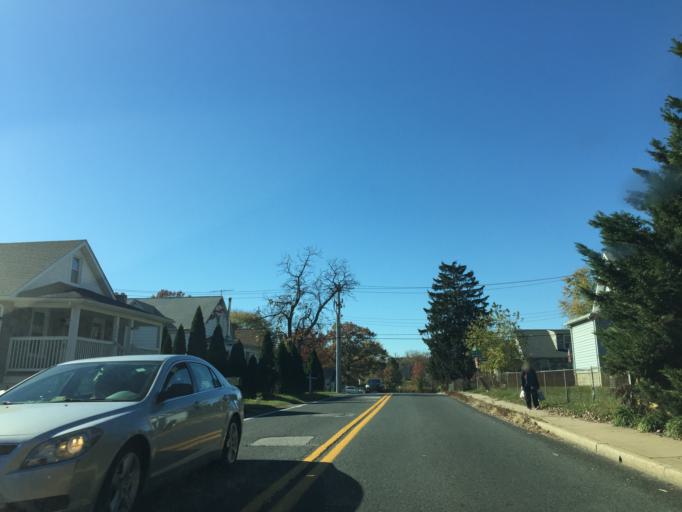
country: US
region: Maryland
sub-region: Baltimore County
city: Baltimore Highlands
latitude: 39.2447
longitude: -76.6451
